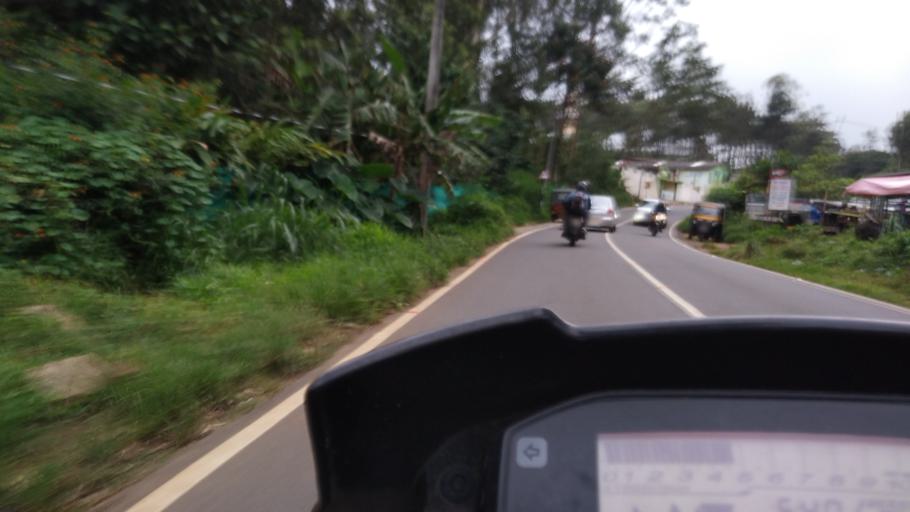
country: IN
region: Tamil Nadu
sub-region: Theni
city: Kombai
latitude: 9.9708
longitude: 77.1904
